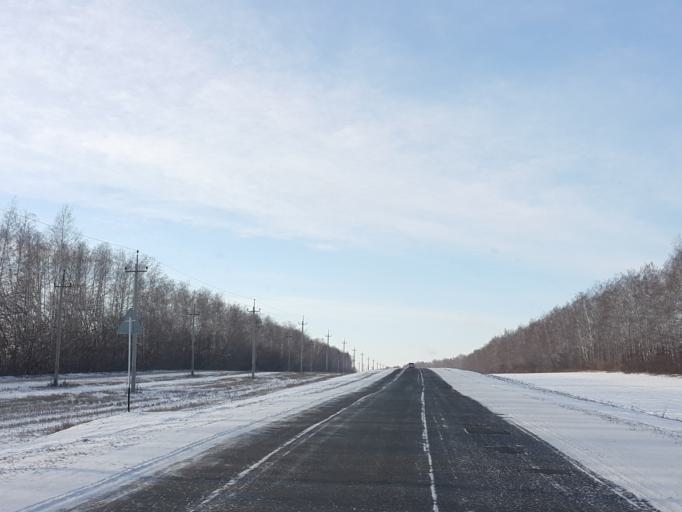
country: RU
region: Tambov
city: Znamenka
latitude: 52.3810
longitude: 41.3245
